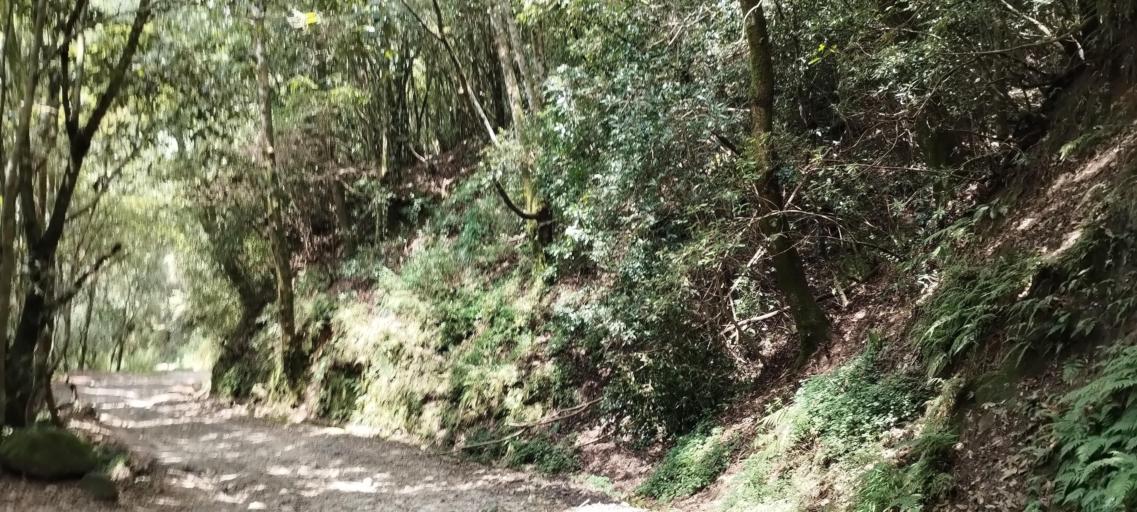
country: NP
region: Central Region
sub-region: Bagmati Zone
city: Kathmandu
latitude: 27.7901
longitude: 85.3747
